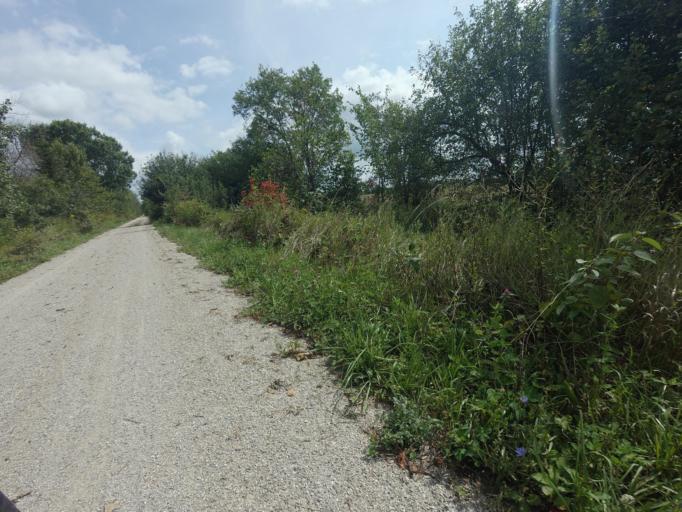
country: CA
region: Ontario
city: North Perth
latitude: 43.5654
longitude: -80.9648
